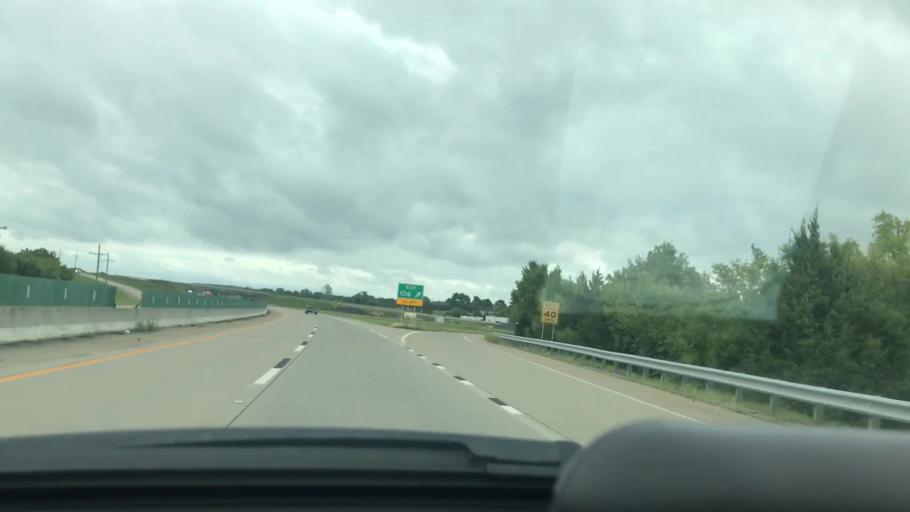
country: US
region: Oklahoma
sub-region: McIntosh County
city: Eufaula
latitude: 35.1279
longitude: -95.6750
